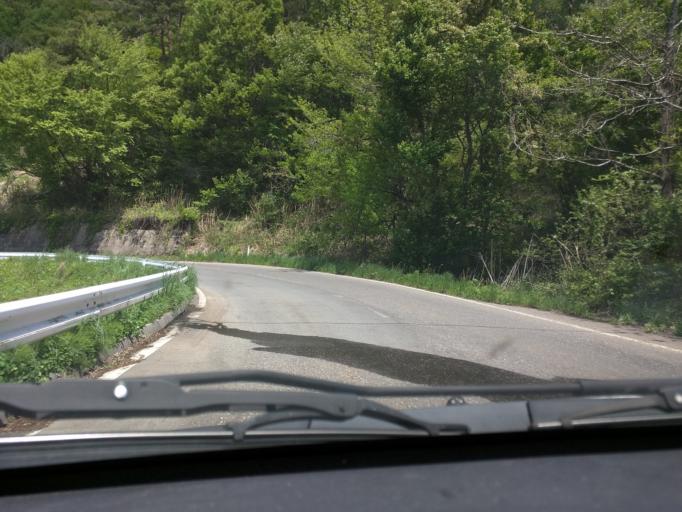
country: JP
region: Fukushima
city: Kitakata
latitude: 37.6392
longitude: 139.8091
